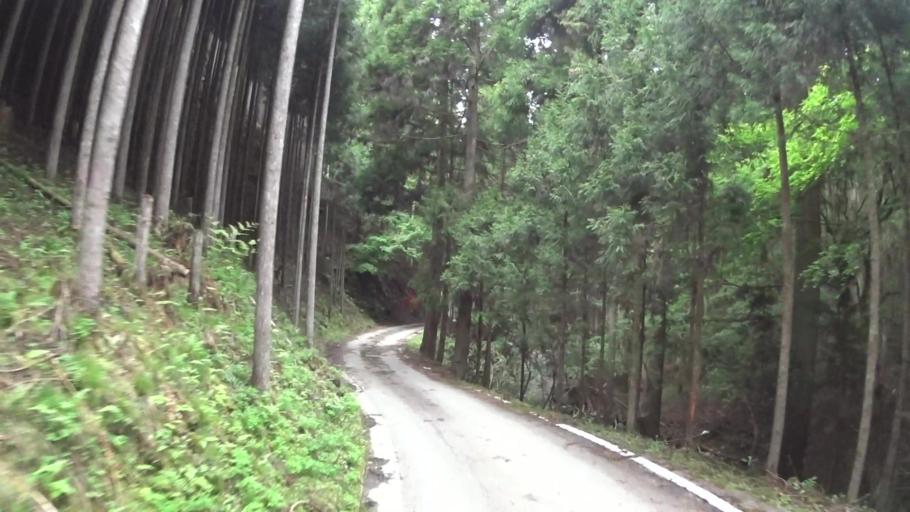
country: JP
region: Kyoto
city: Kameoka
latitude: 35.1058
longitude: 135.6310
